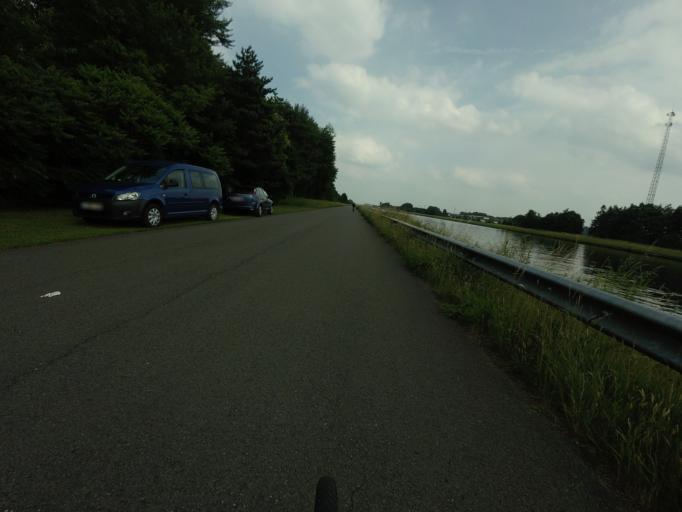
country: BE
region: Flanders
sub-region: Provincie Antwerpen
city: Schilde
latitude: 51.2145
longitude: 4.5782
